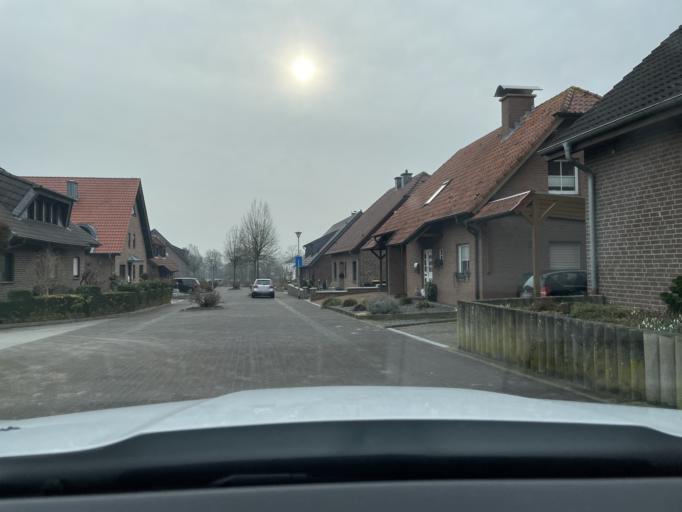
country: DE
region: North Rhine-Westphalia
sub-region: Regierungsbezirk Dusseldorf
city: Wachtendonk
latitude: 51.4027
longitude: 6.3096
